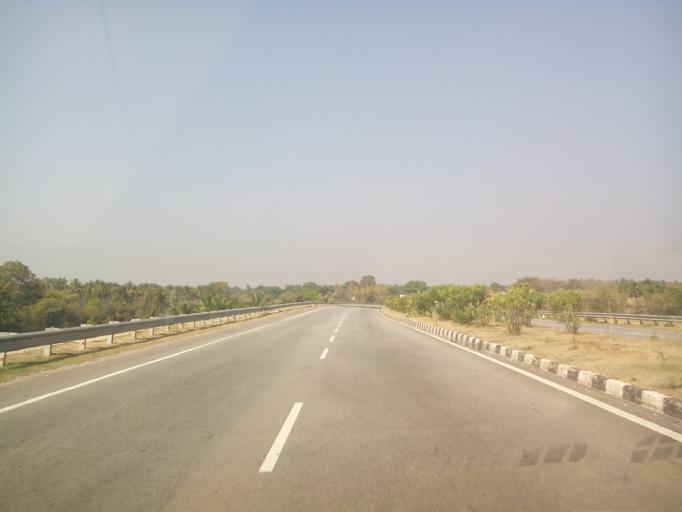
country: IN
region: Karnataka
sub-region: Tumkur
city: Kunigal
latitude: 13.0029
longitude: 76.9713
